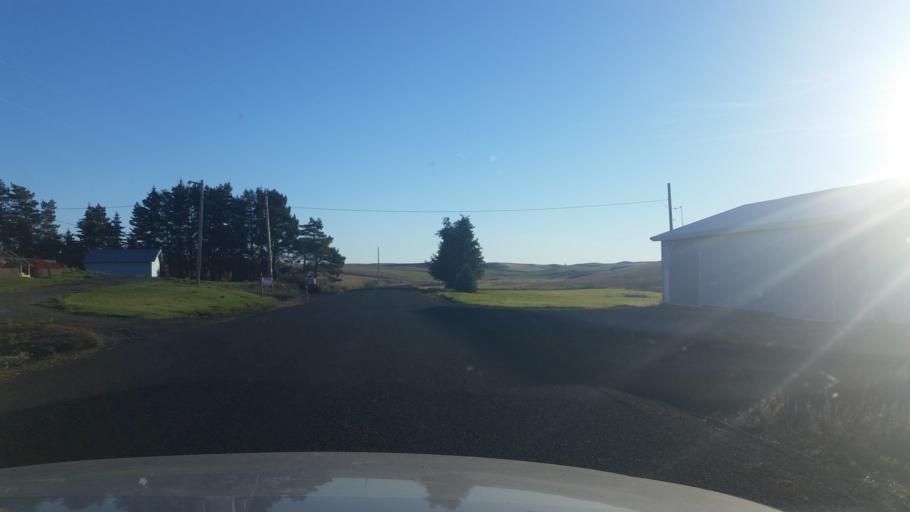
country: US
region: Washington
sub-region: Spokane County
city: Cheney
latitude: 47.3554
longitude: -117.4495
